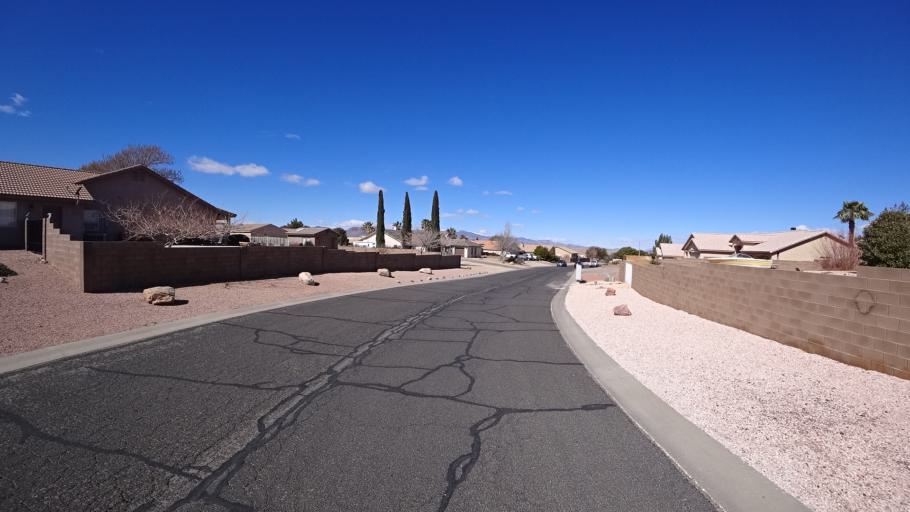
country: US
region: Arizona
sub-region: Mohave County
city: Kingman
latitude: 35.2035
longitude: -113.9740
